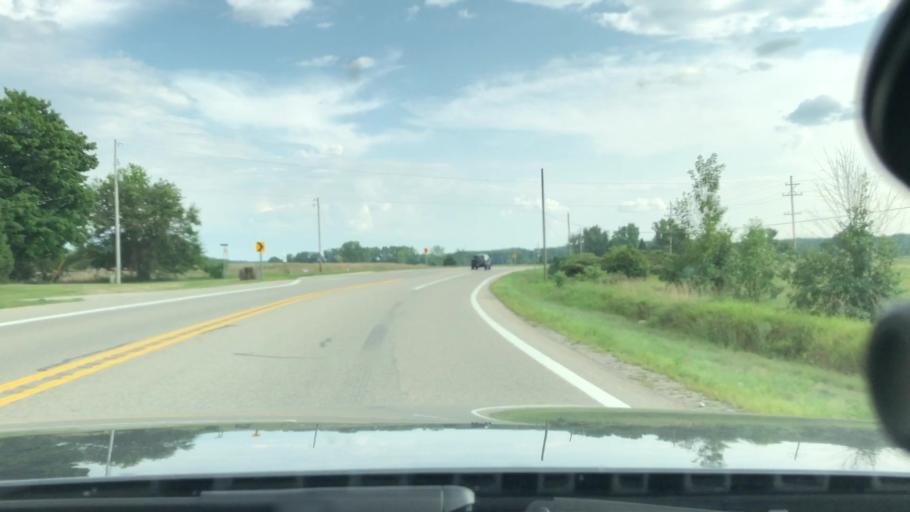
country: US
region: Michigan
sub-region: Washtenaw County
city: Chelsea
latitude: 42.2485
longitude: -84.0334
